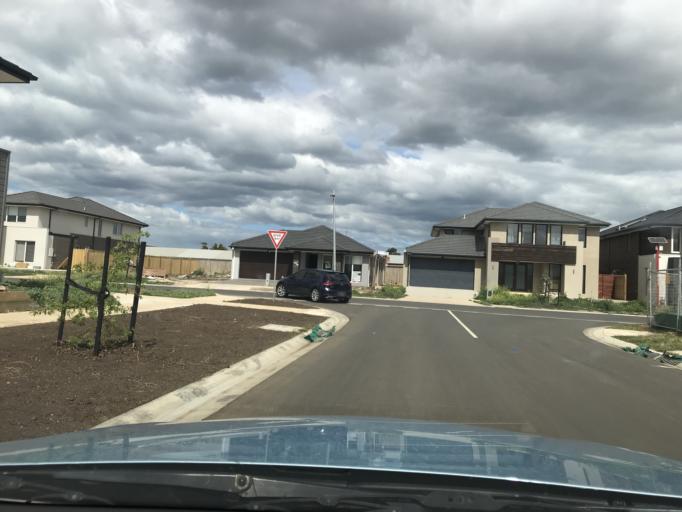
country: AU
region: Victoria
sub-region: Wyndham
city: Williams Landing
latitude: -37.8656
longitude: 144.7530
